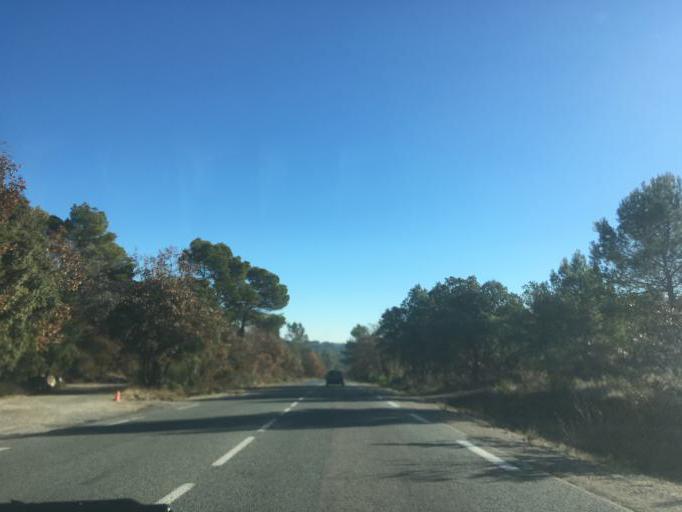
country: FR
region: Provence-Alpes-Cote d'Azur
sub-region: Departement du Var
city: Lorgues
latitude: 43.5456
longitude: 6.3388
